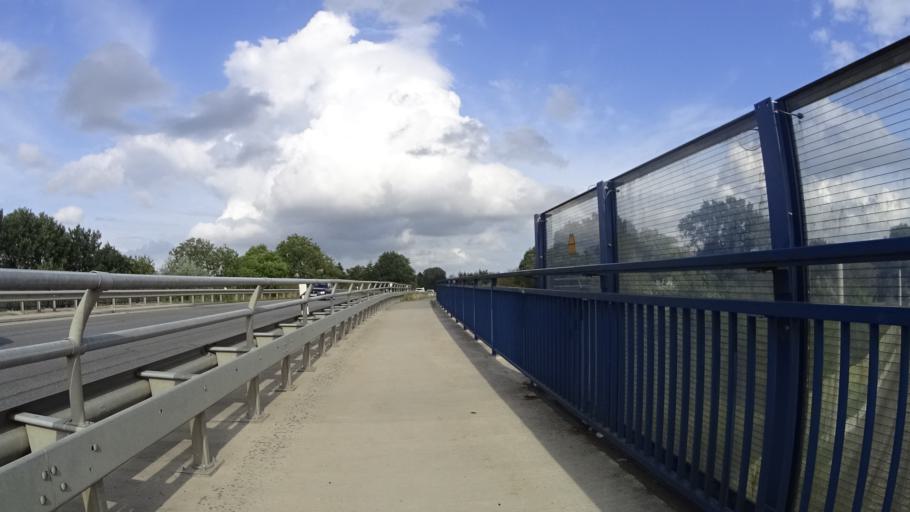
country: DE
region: Lower Saxony
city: Varel
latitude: 53.3905
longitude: 8.1633
